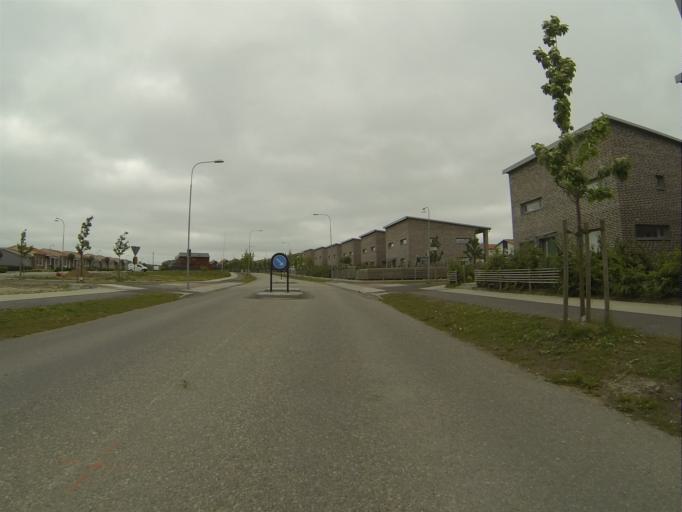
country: SE
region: Skane
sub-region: Lunds Kommun
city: Genarp
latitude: 55.6586
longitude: 13.3557
